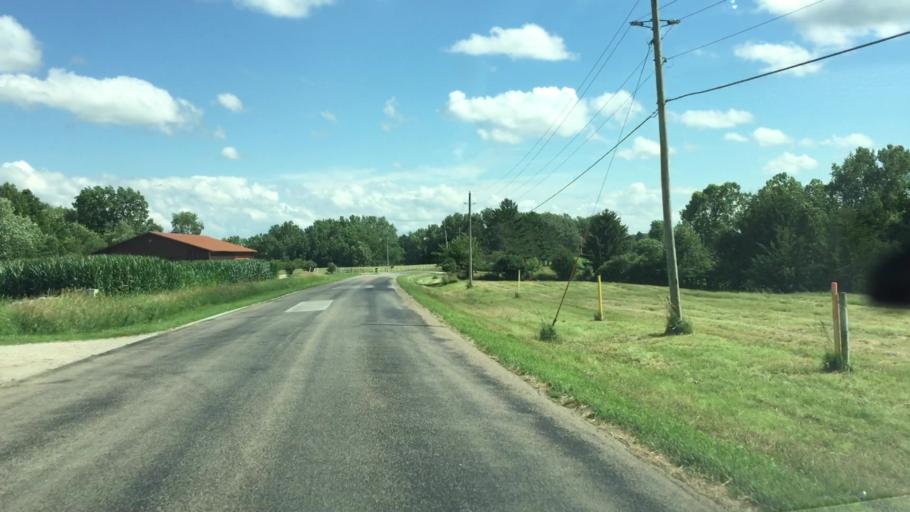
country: US
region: Iowa
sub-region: Johnson County
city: North Liberty
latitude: 41.8130
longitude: -91.6152
